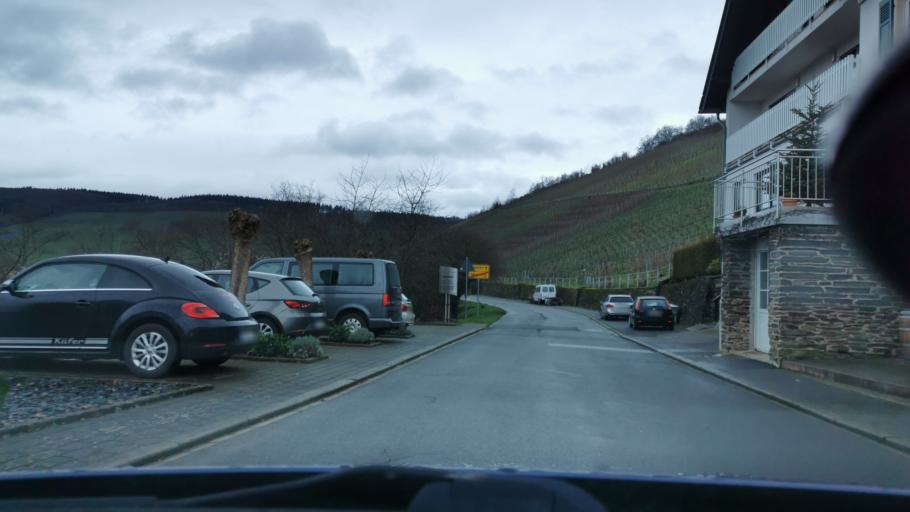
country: DE
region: Rheinland-Pfalz
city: Maring-Noviand
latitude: 49.9287
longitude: 7.0006
